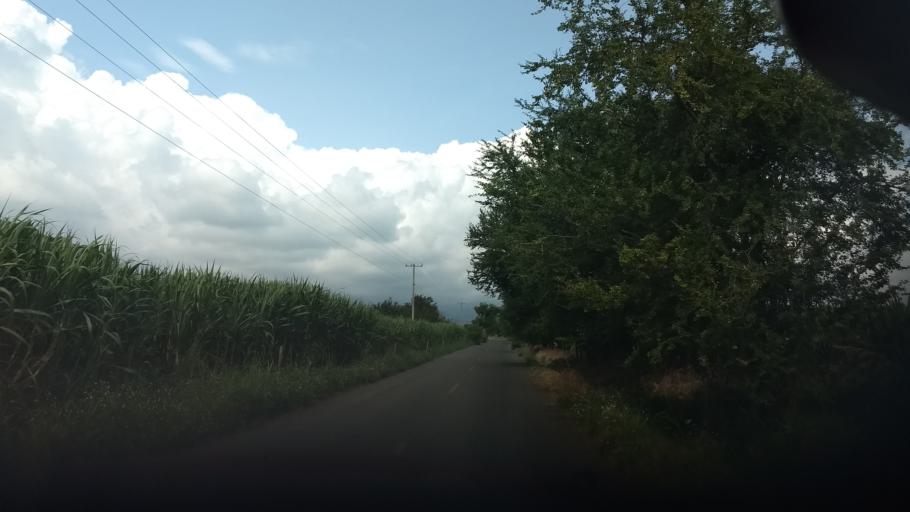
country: MX
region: Jalisco
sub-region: Tonila
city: San Marcos
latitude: 19.4249
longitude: -103.4908
